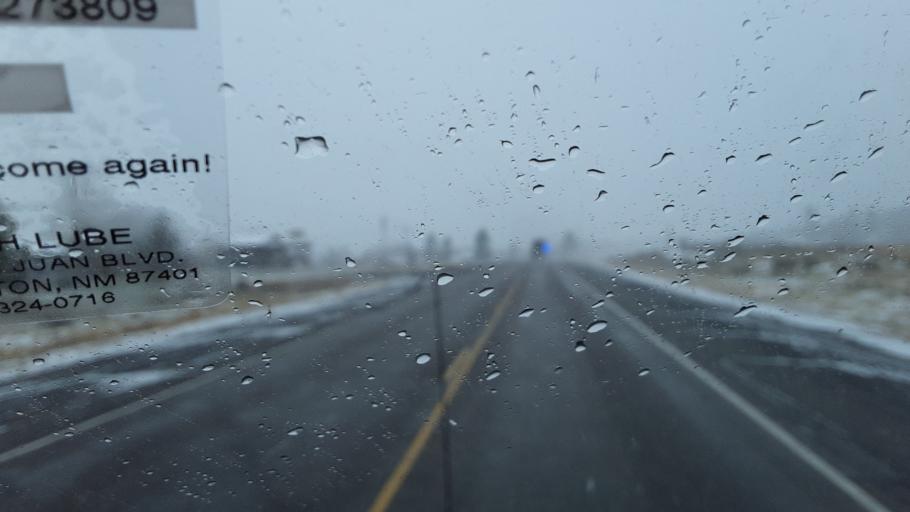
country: US
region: New Mexico
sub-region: Rio Arriba County
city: Chama
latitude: 36.8550
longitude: -106.5758
